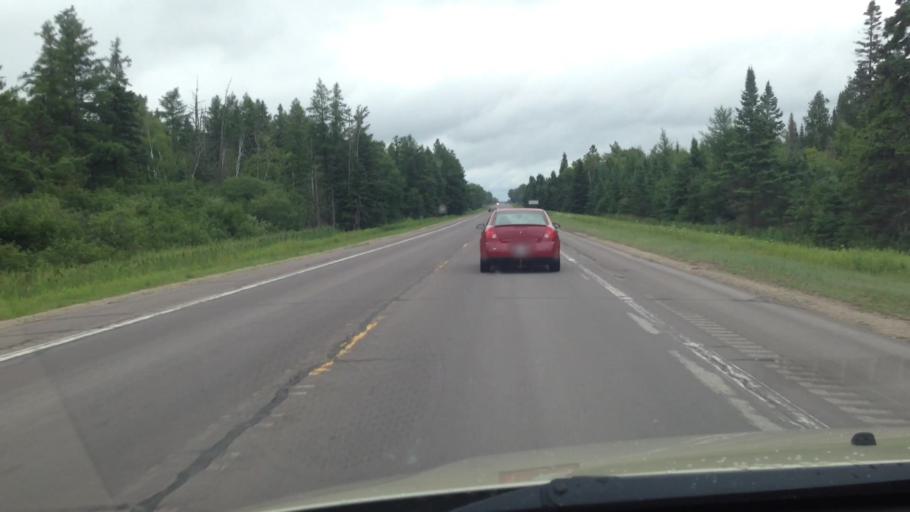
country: US
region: Michigan
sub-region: Schoolcraft County
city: Manistique
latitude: 45.9982
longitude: -86.0042
